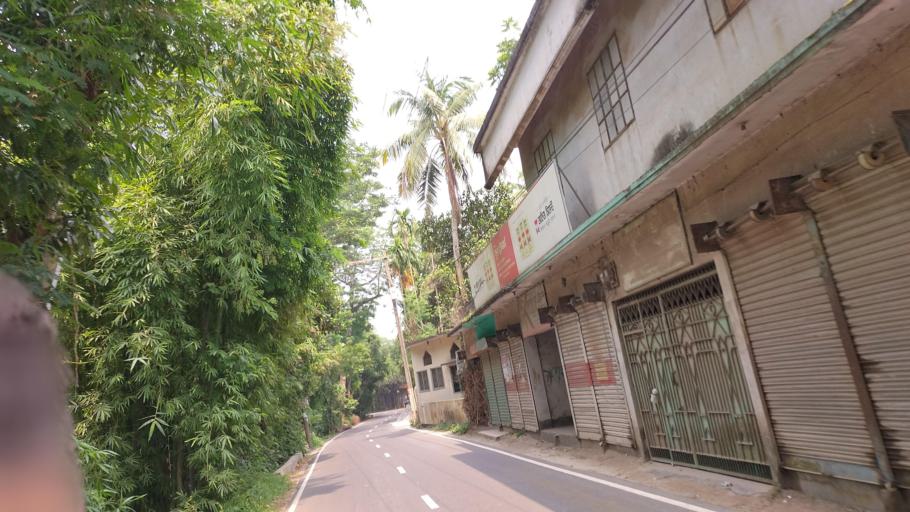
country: BD
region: Dhaka
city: Azimpur
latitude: 23.7139
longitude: 90.2814
